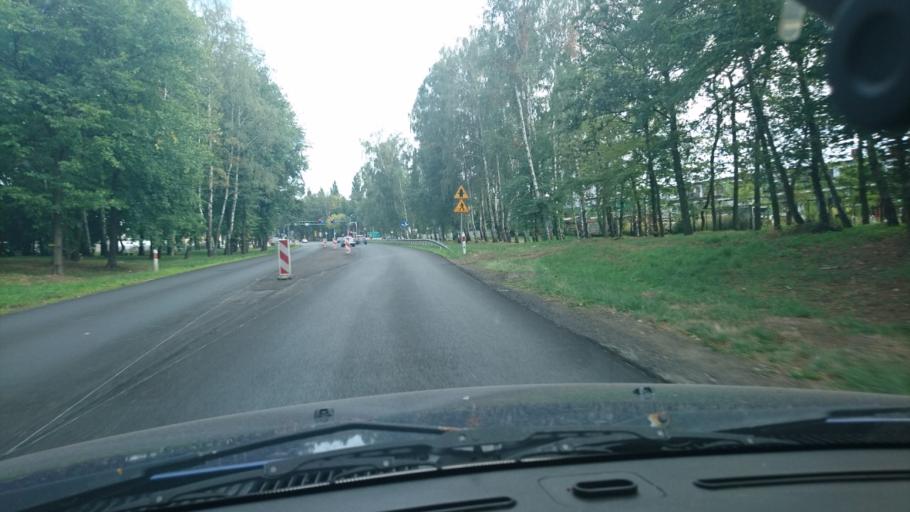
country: PL
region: Greater Poland Voivodeship
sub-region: Powiat ostrzeszowski
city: Ostrzeszow
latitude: 51.4229
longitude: 17.9246
